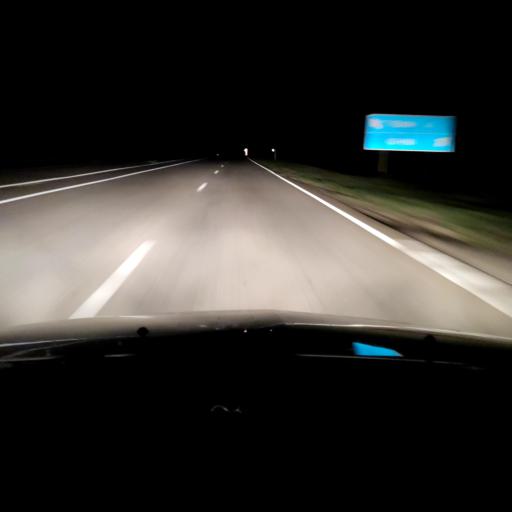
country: RU
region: Belgorod
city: Skorodnoye
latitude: 50.9899
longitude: 37.2039
